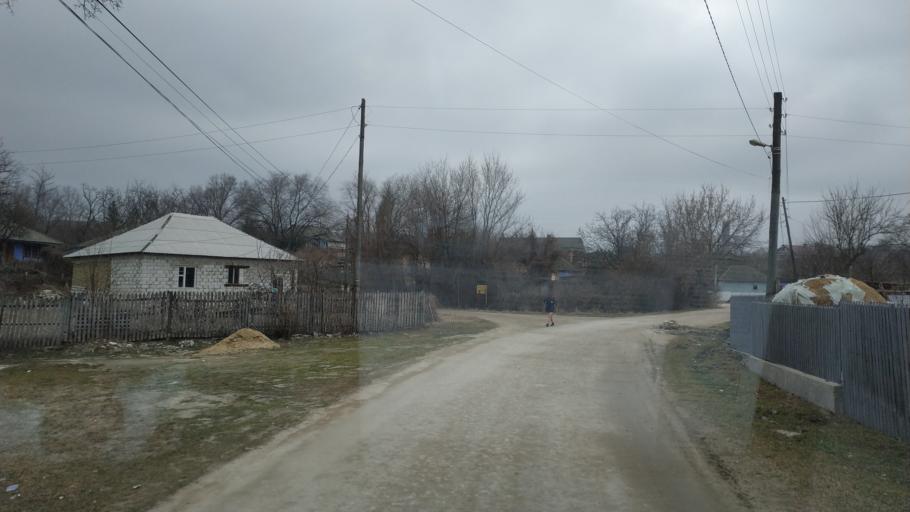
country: MD
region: Hincesti
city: Hincesti
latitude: 46.8823
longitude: 28.4090
